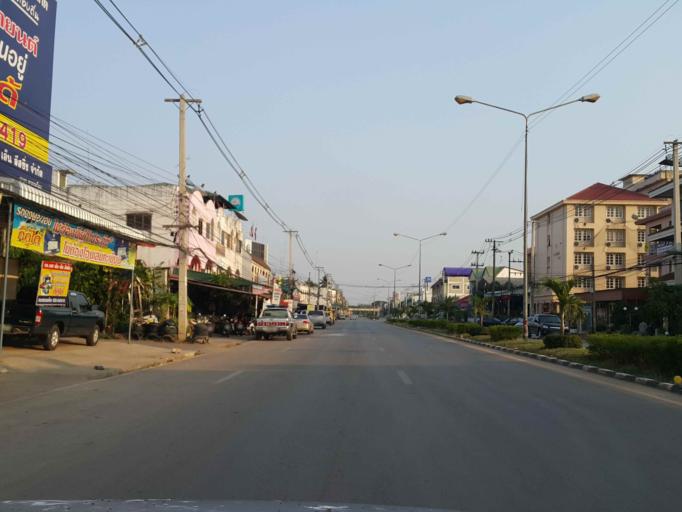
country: TH
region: Sukhothai
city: Sawankhalok
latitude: 17.3007
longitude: 99.8348
